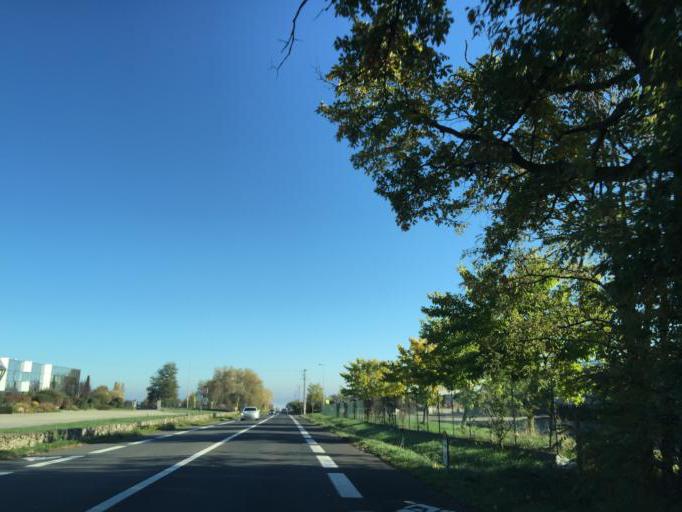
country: FR
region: Rhone-Alpes
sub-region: Departement du Rhone
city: Taluyers
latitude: 45.6377
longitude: 4.7366
